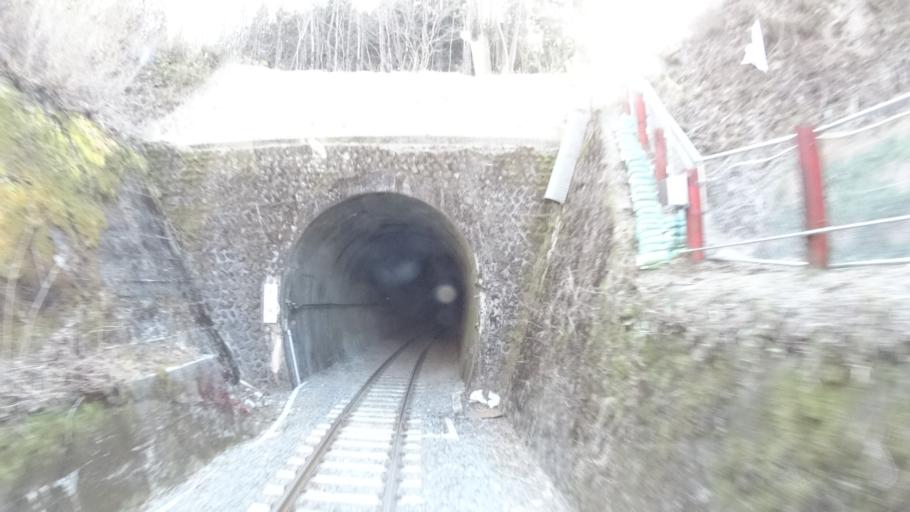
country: JP
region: Iwate
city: Yamada
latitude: 39.4927
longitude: 141.9267
